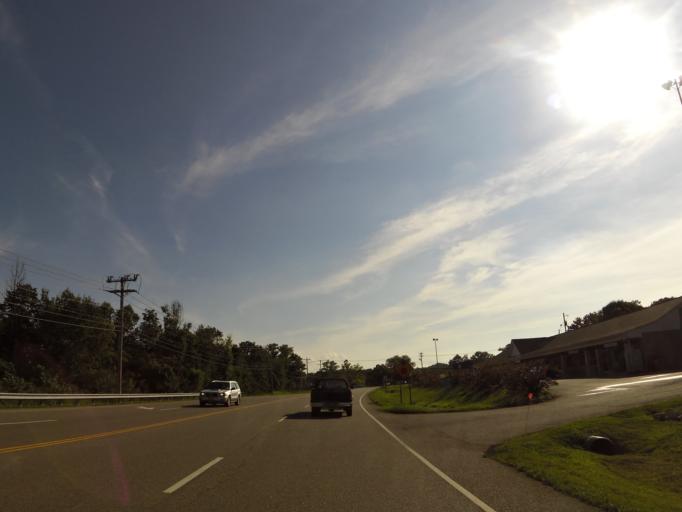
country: US
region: Tennessee
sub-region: Blount County
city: Louisville
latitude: 35.8183
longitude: -84.0276
